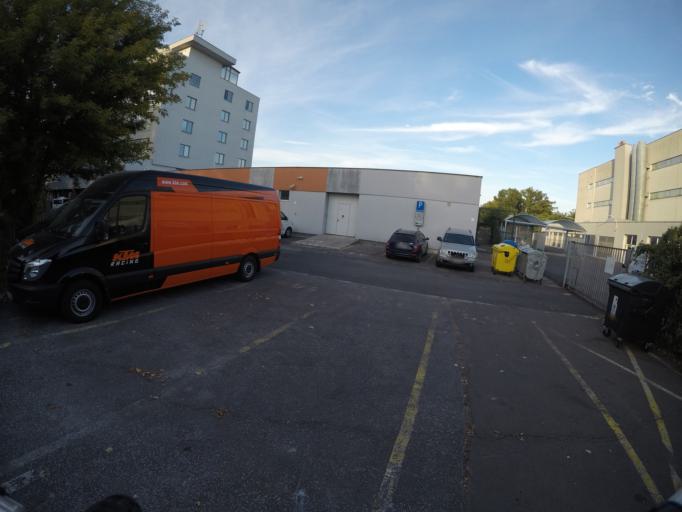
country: SK
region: Bratislavsky
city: Bratislava
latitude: 48.1795
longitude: 17.1705
